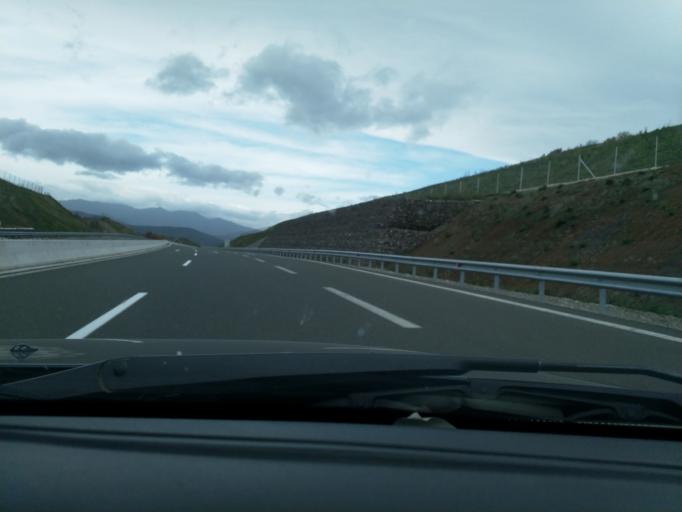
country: GR
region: Thessaly
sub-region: Nomos Kardhitsas
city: Anavra
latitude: 39.1542
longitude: 22.1228
